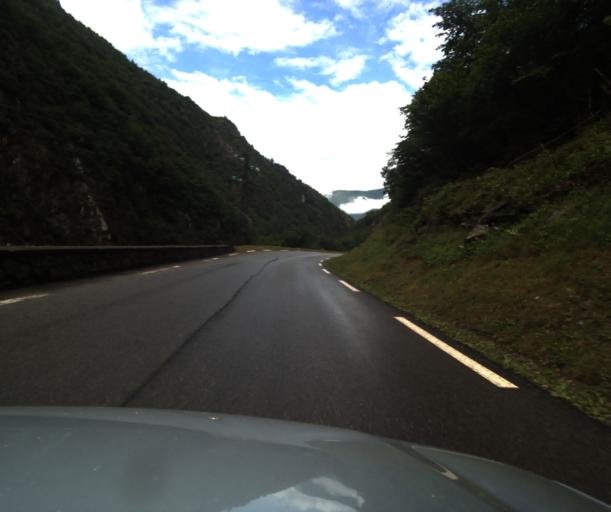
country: FR
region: Midi-Pyrenees
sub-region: Departement des Hautes-Pyrenees
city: Luz-Saint-Sauveur
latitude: 42.8471
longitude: -0.0069
